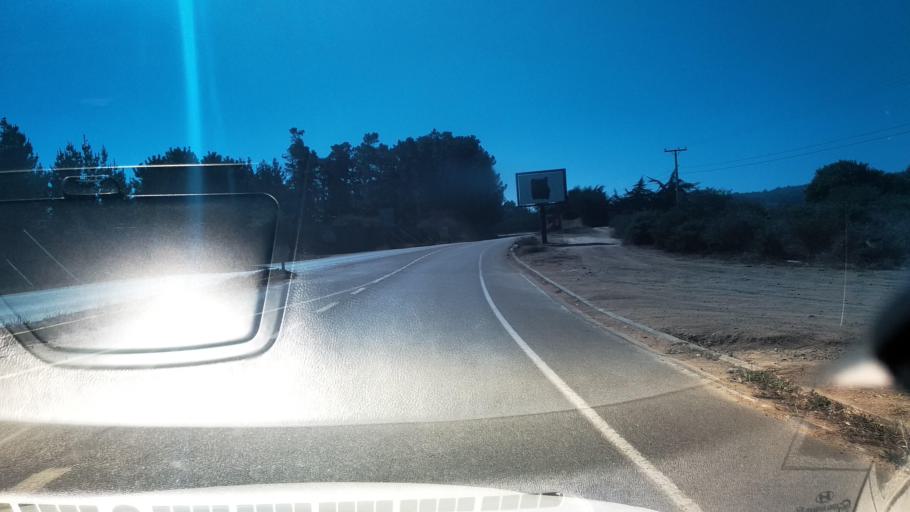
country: CL
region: O'Higgins
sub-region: Provincia de Colchagua
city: Santa Cruz
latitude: -34.4648
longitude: -72.0231
